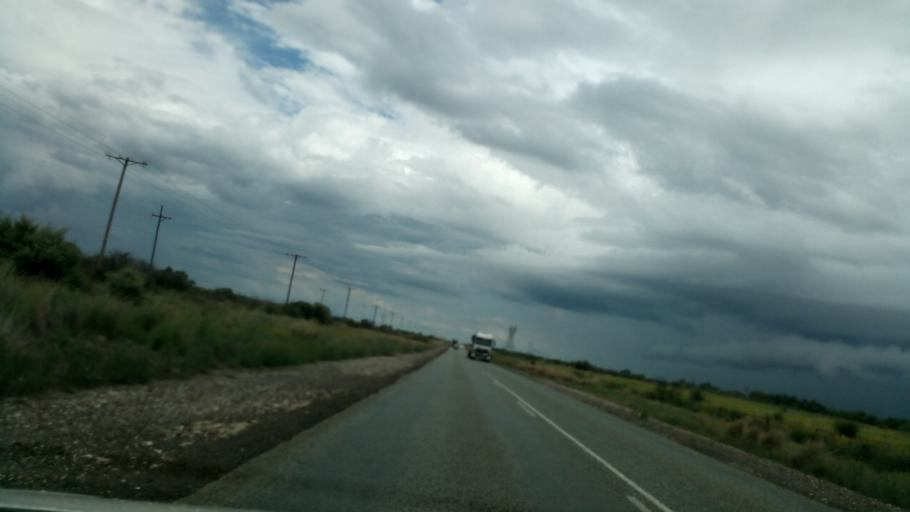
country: ZA
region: Northern Cape
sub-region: Siyanda District Municipality
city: Danielskuil
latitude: -28.2614
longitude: 24.0594
